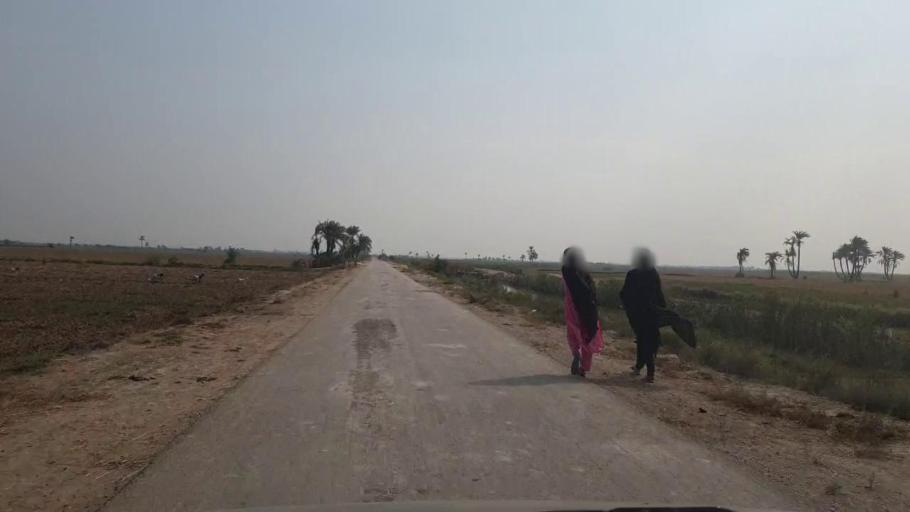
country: PK
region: Sindh
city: Tando Muhammad Khan
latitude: 25.1027
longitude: 68.3725
